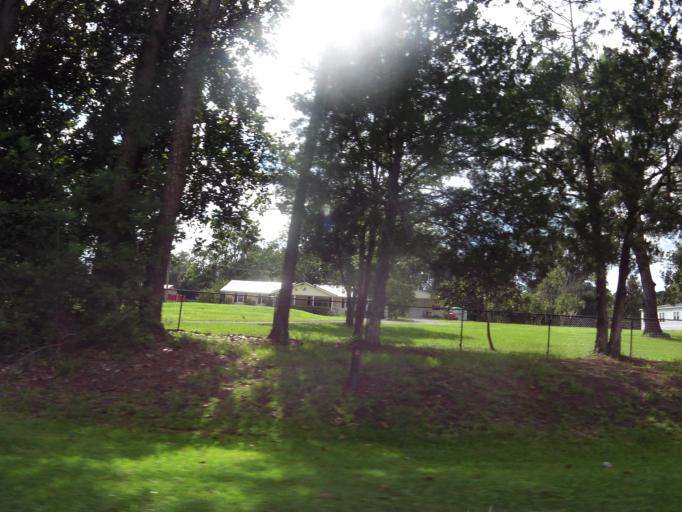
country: US
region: Florida
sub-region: Clay County
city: Green Cove Springs
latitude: 29.9635
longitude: -81.6936
